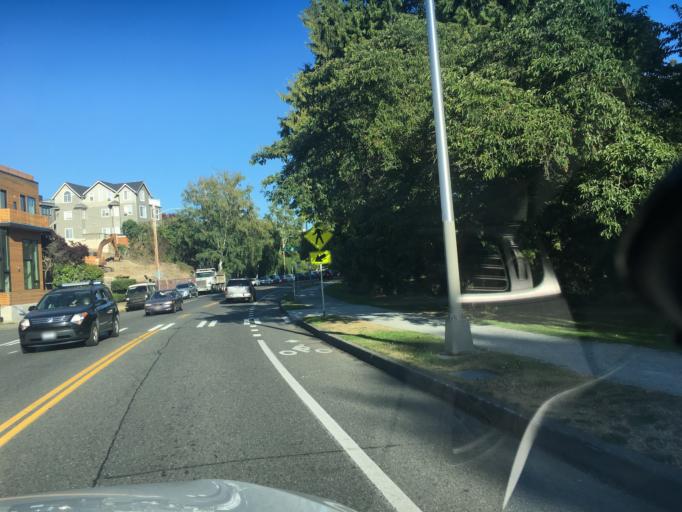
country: US
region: Washington
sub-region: King County
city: Shoreline
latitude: 47.6827
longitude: -122.3301
